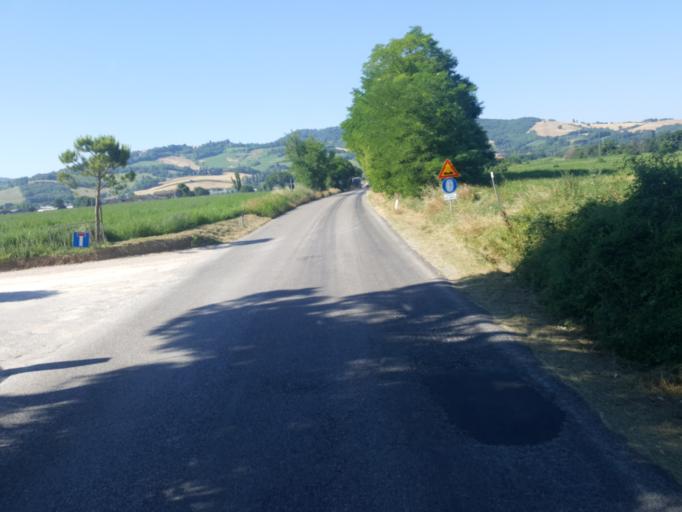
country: IT
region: The Marches
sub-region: Provincia di Pesaro e Urbino
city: Padiglione
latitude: 43.8459
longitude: 12.7206
